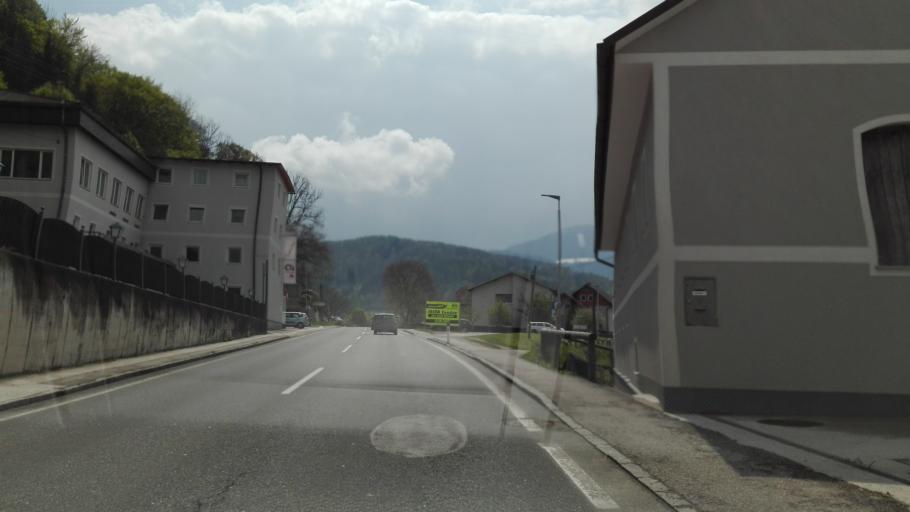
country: AT
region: Upper Austria
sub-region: Politischer Bezirk Steyr-Land
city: Ternberg
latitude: 47.9502
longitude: 14.3593
